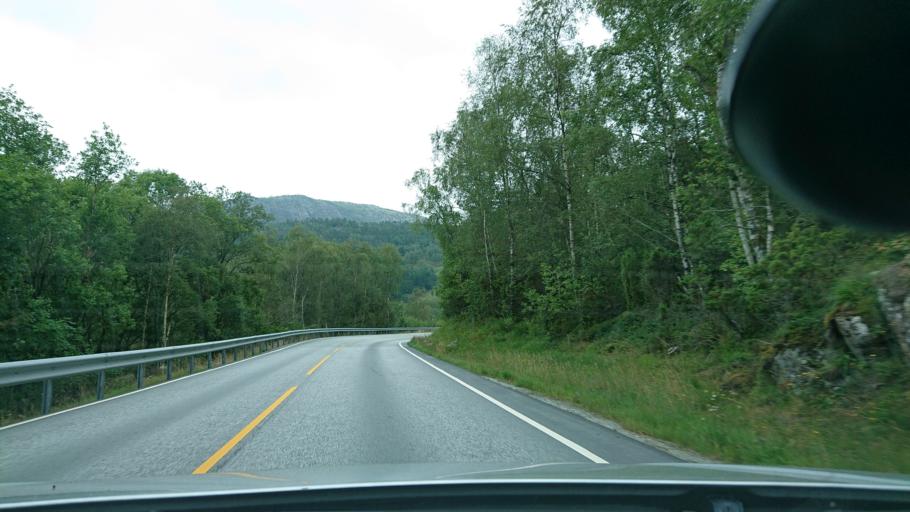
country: NO
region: Rogaland
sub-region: Hjelmeland
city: Hjelmelandsvagen
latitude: 59.1655
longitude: 6.1545
